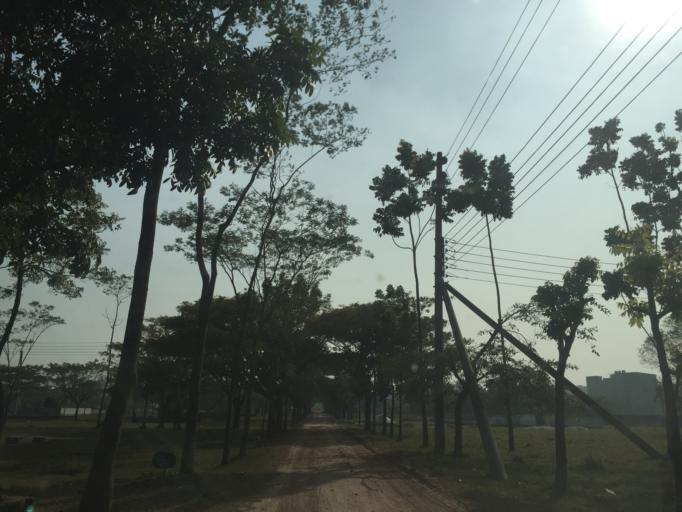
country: BD
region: Dhaka
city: Tungi
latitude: 23.8726
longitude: 90.3129
